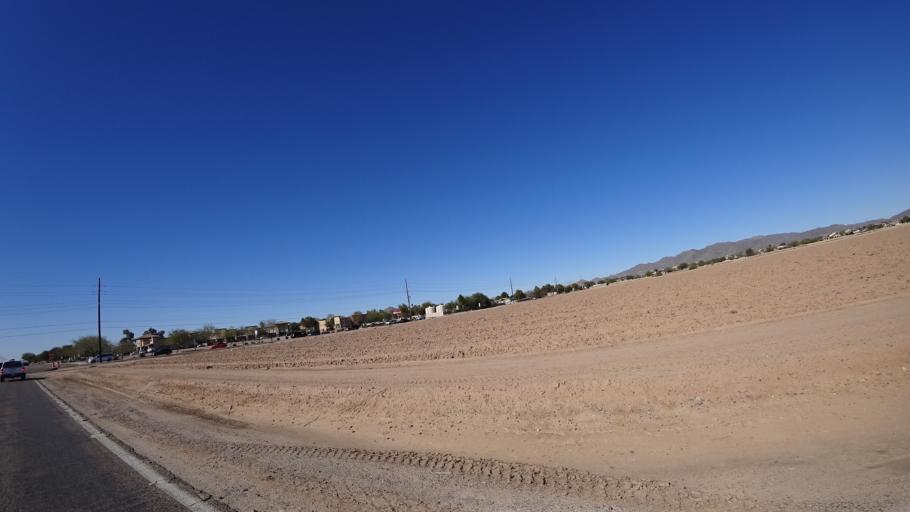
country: US
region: Arizona
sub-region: Maricopa County
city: Buckeye
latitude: 33.4065
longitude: -112.5898
